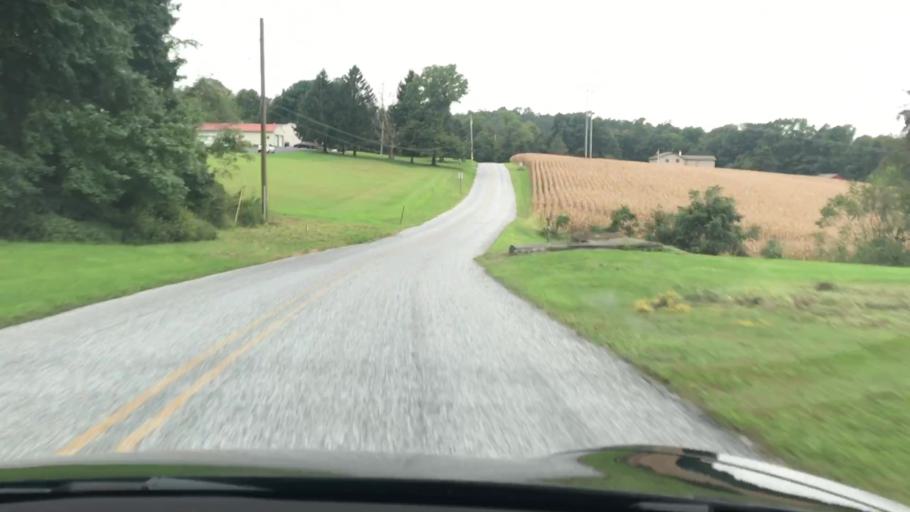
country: US
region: Pennsylvania
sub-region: York County
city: Dillsburg
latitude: 40.1132
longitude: -76.9590
